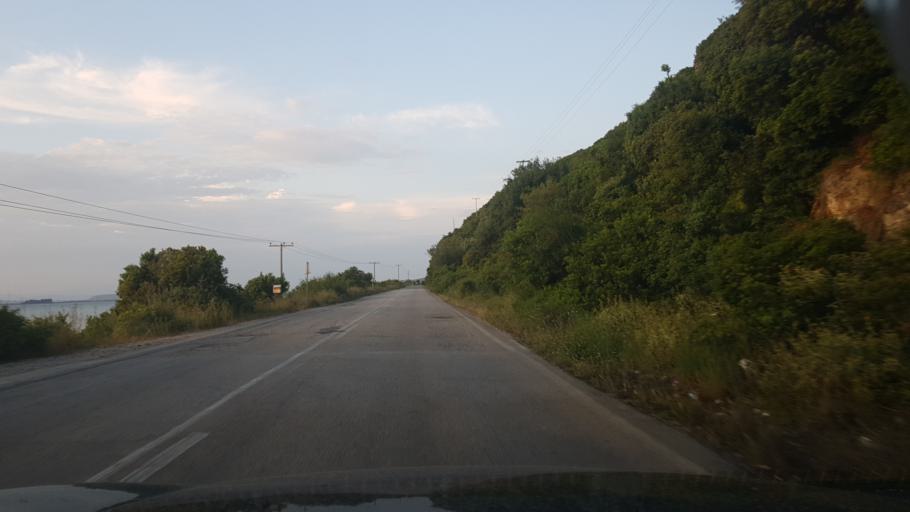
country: GR
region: Ionian Islands
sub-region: Lefkada
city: Lefkada
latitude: 38.8554
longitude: 20.7489
